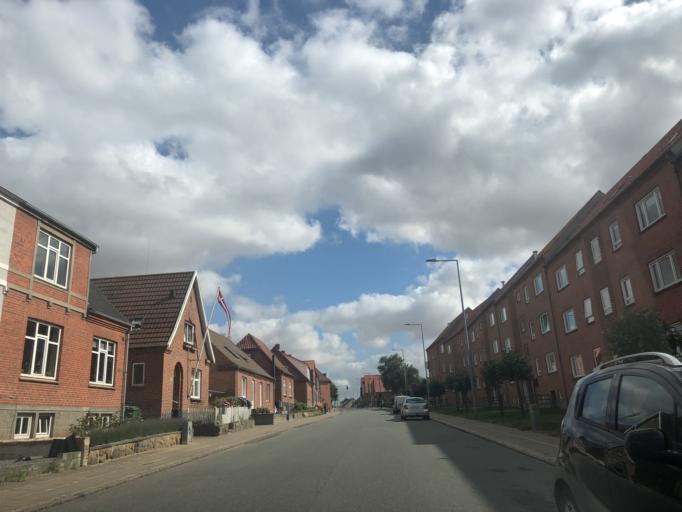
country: DK
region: Central Jutland
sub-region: Struer Kommune
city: Struer
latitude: 56.4882
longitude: 8.5997
